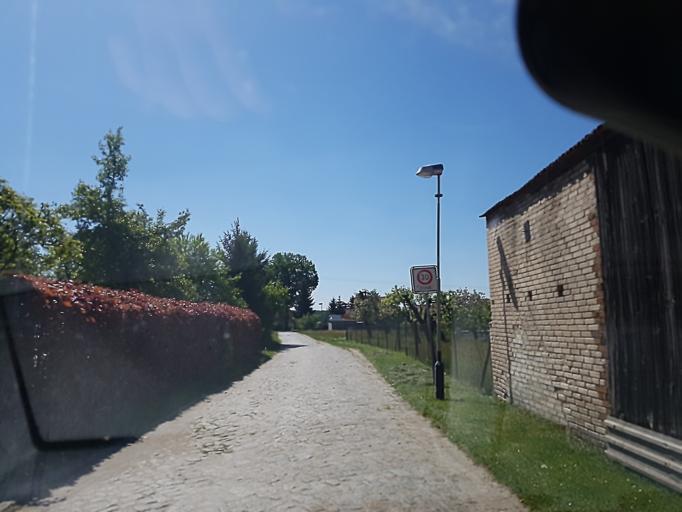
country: DE
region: Brandenburg
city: Sallgast
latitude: 51.6174
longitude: 13.8097
